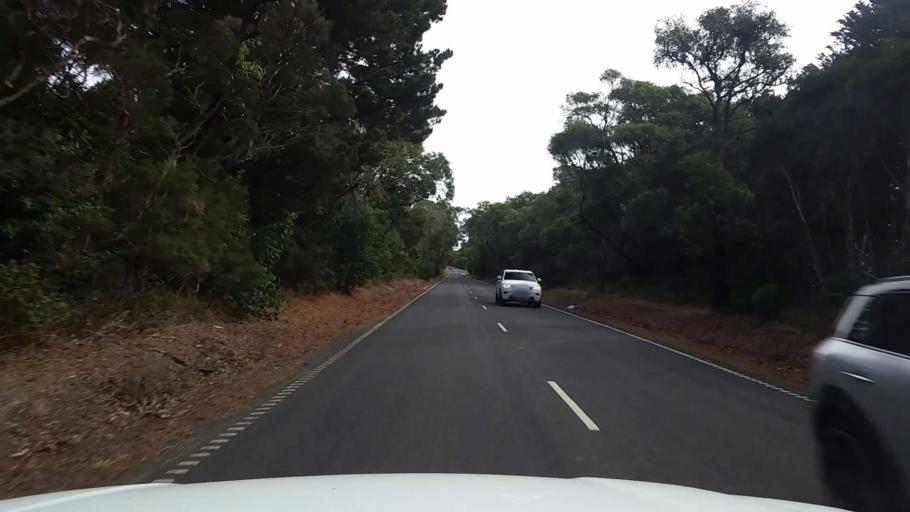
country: AU
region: Victoria
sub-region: Mornington Peninsula
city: Balnarring
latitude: -38.3211
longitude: 145.0905
